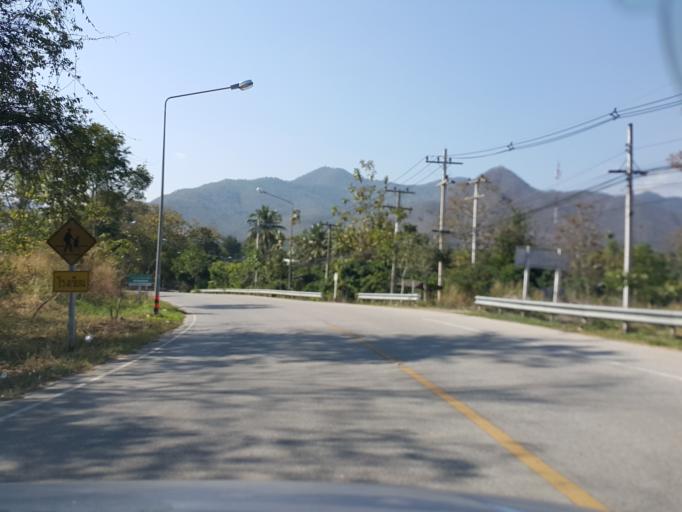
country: TH
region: Chiang Mai
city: Mae Wang
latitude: 18.6168
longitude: 98.7735
